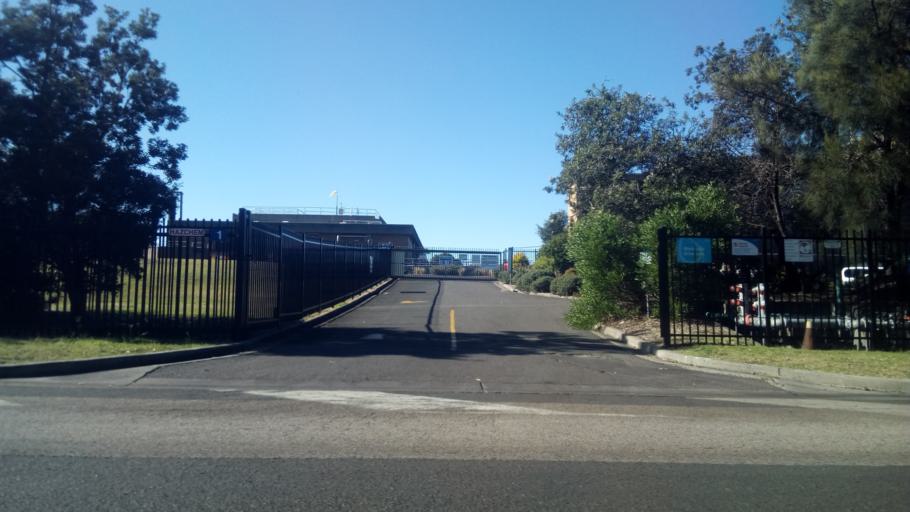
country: AU
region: New South Wales
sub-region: Wollongong
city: Coniston
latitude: -34.4411
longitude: 150.8967
